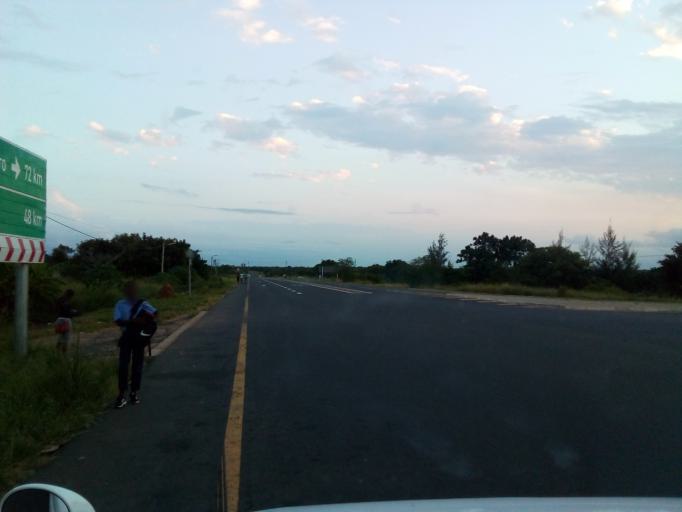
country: MZ
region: Maputo City
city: Maputo
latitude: -26.3264
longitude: 32.6609
